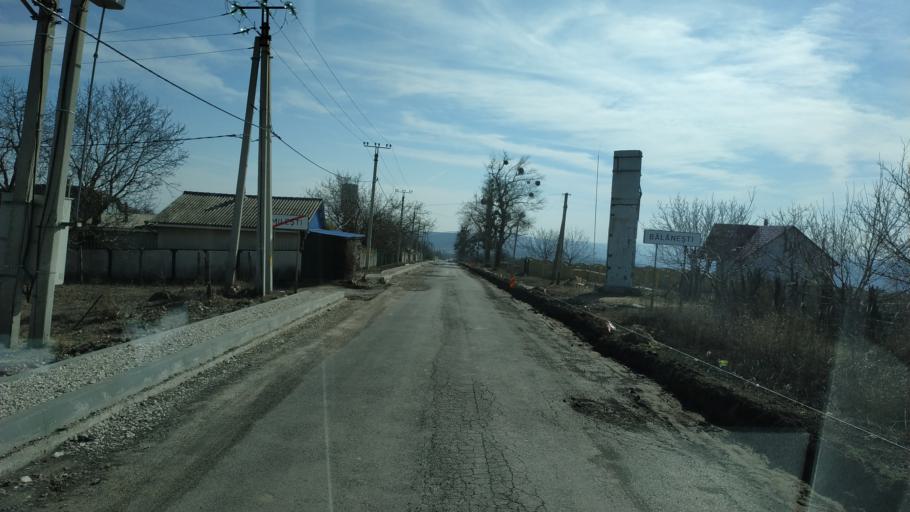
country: MD
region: Nisporeni
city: Nisporeni
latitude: 47.2139
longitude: 28.0558
